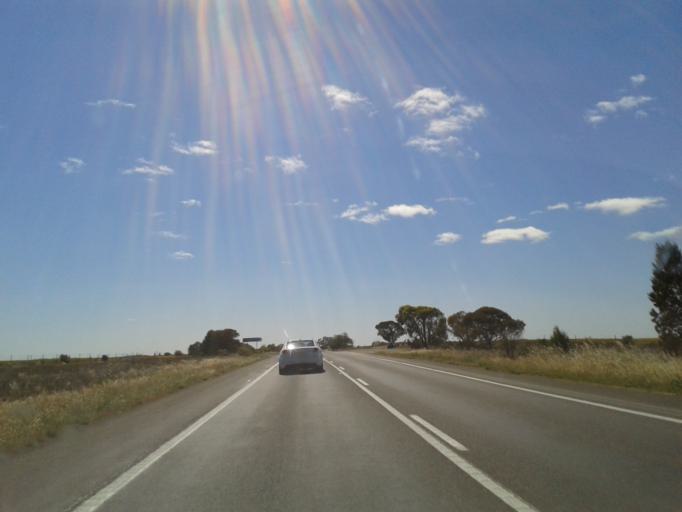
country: AU
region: New South Wales
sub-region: Wentworth
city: Dareton
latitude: -34.2498
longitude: 141.9325
